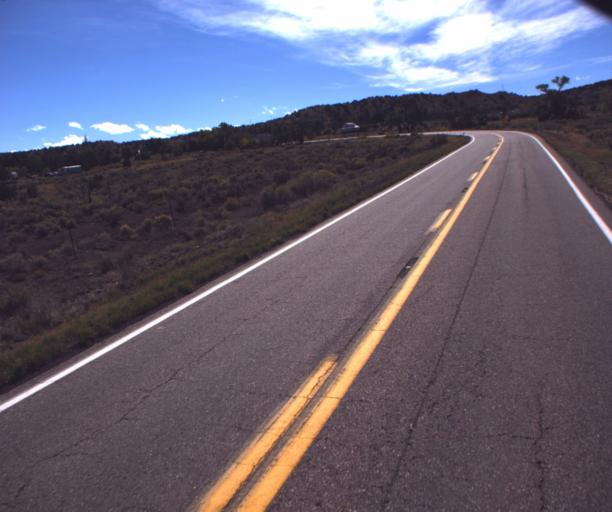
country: US
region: Arizona
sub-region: Apache County
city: Saint Johns
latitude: 34.4683
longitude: -109.6159
